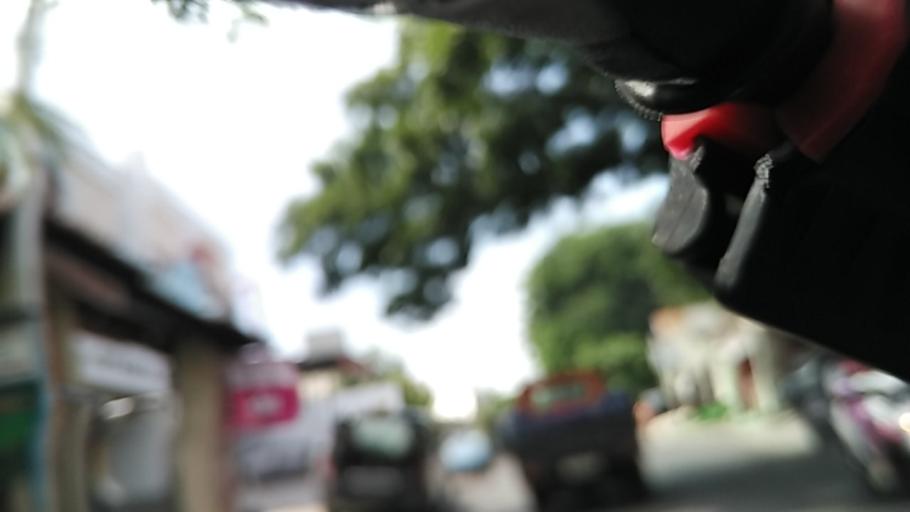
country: ID
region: Central Java
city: Semarang
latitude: -7.0088
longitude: 110.4268
